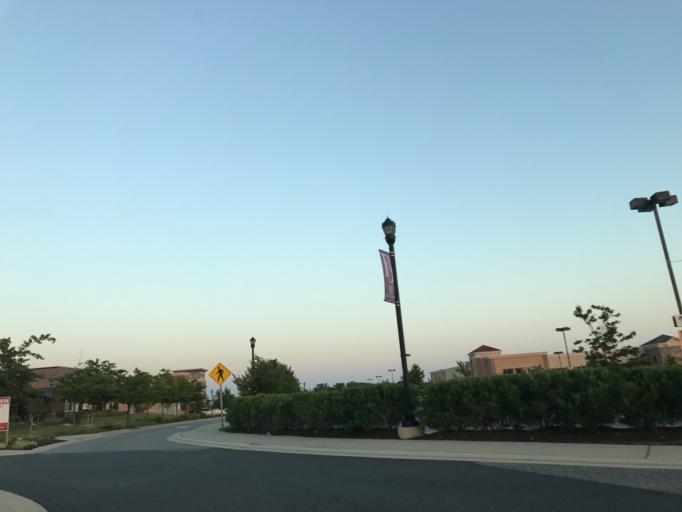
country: US
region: Maryland
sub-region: Harford County
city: Bel Air South
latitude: 39.4682
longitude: -76.3092
